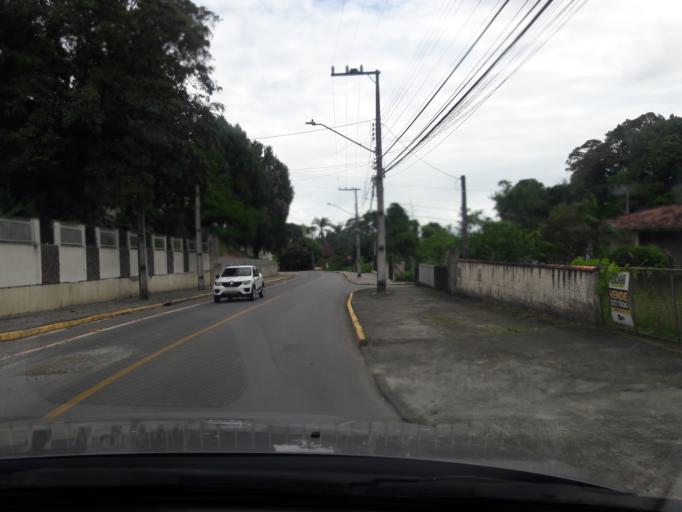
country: BR
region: Santa Catarina
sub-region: Joinville
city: Joinville
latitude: -26.3198
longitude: -48.8617
